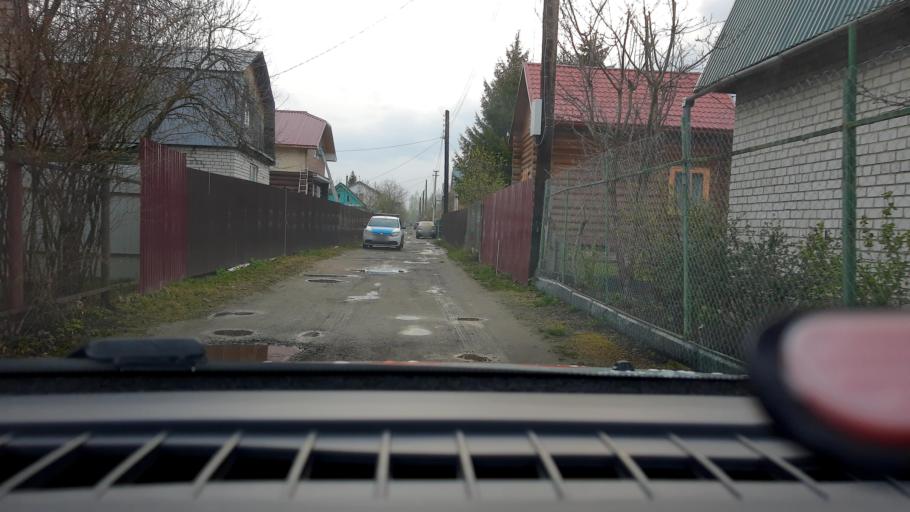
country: RU
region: Nizjnij Novgorod
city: Gorbatovka
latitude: 56.2988
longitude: 43.7682
